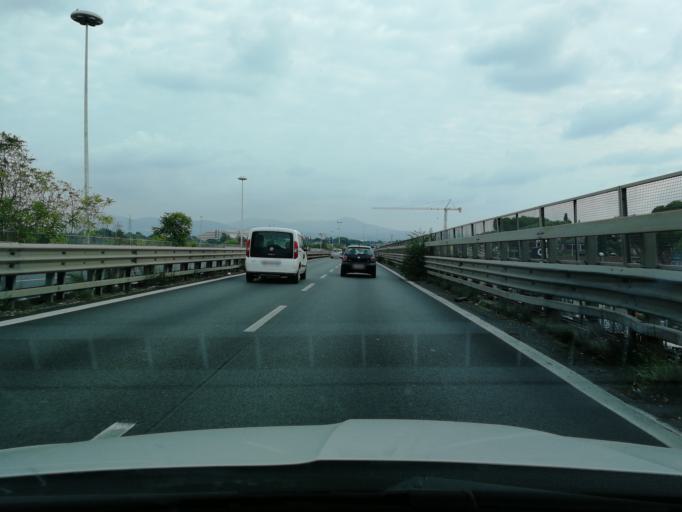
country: IT
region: Latium
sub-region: Citta metropolitana di Roma Capitale
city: Ciampino
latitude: 41.8424
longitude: 12.5847
